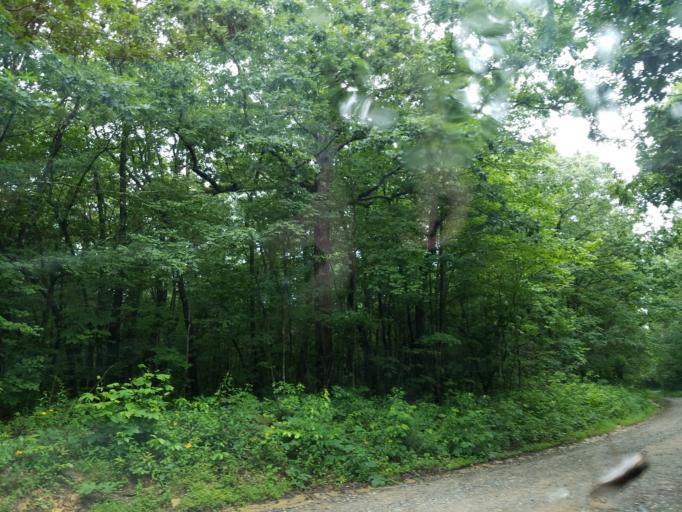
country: US
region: Georgia
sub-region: Lumpkin County
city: Dahlonega
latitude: 34.6471
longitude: -84.1576
